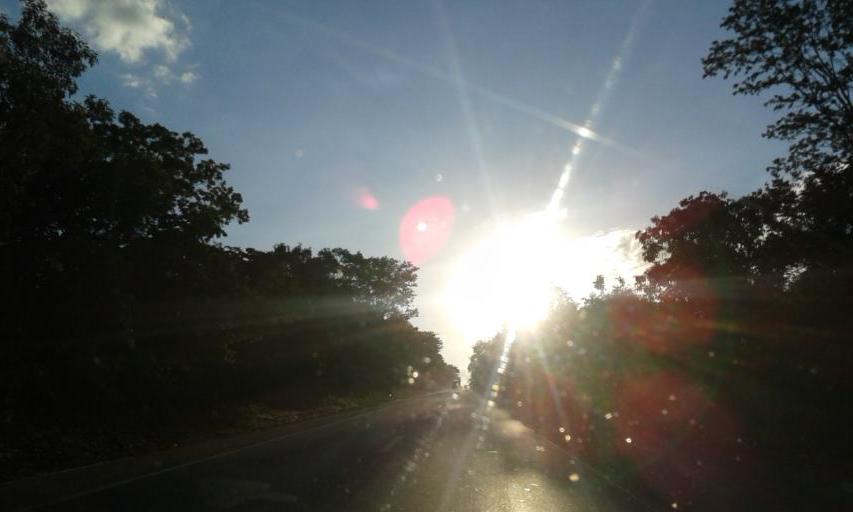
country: BR
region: Minas Gerais
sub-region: Bom Despacho
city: Bom Despacho
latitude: -19.7856
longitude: -45.2869
